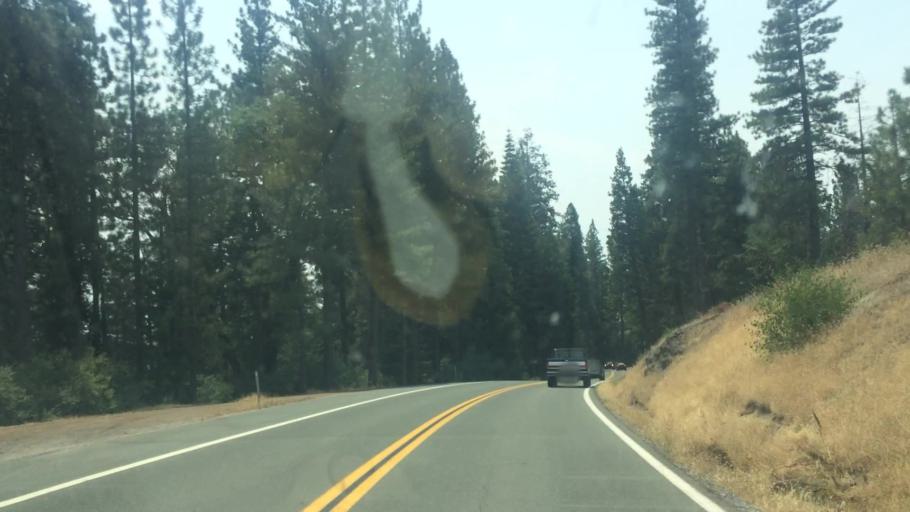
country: US
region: California
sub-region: Amador County
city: Pioneer
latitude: 38.5239
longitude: -120.4459
